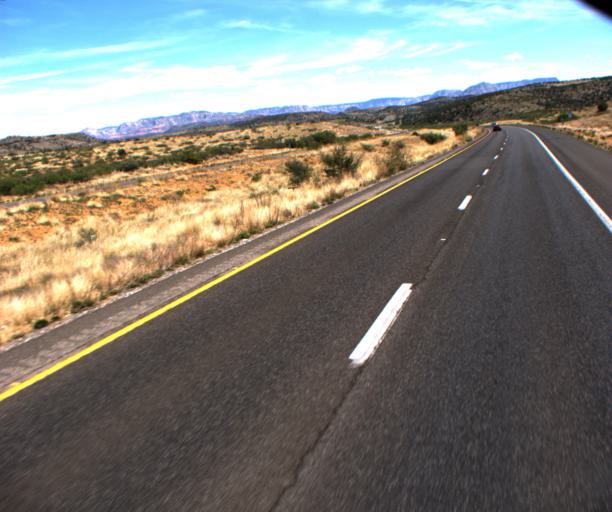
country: US
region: Arizona
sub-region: Yavapai County
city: Cornville
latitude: 34.7735
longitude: -111.9322
